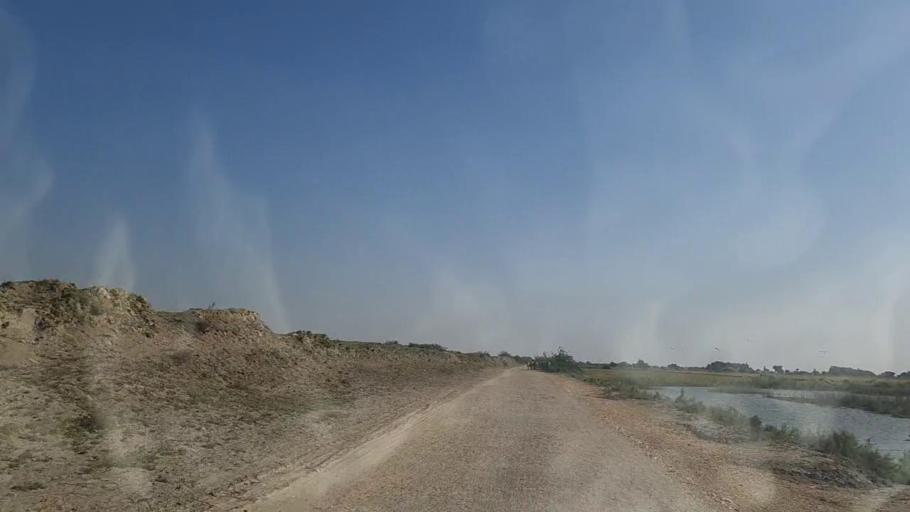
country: PK
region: Sindh
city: Mirpur Batoro
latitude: 24.6078
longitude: 68.1710
